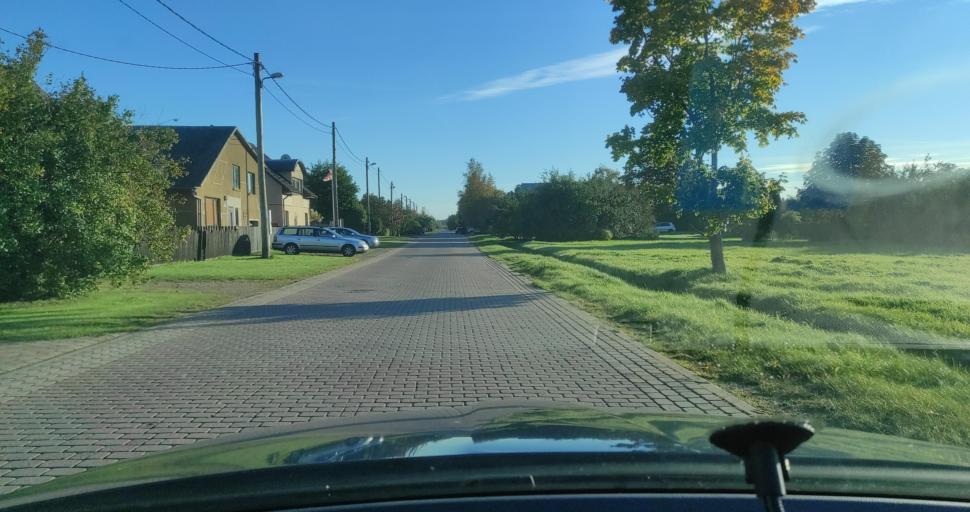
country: LV
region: Ventspils
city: Ventspils
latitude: 57.3727
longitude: 21.5769
